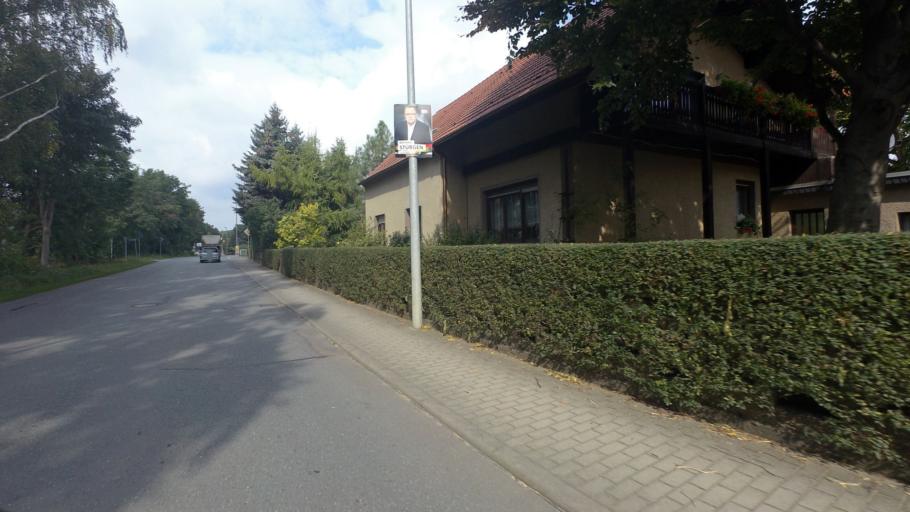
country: DE
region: Brandenburg
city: Bad Liebenwerda
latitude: 51.5187
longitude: 13.4164
